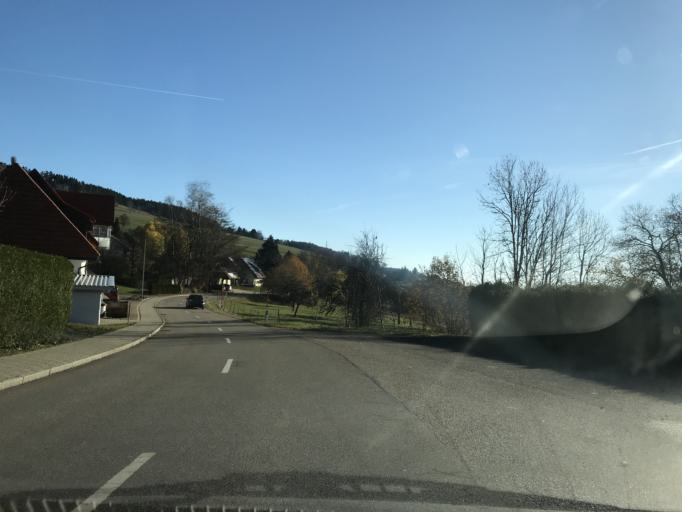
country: DE
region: Baden-Wuerttemberg
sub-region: Freiburg Region
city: Rickenbach
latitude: 47.6368
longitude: 7.9782
